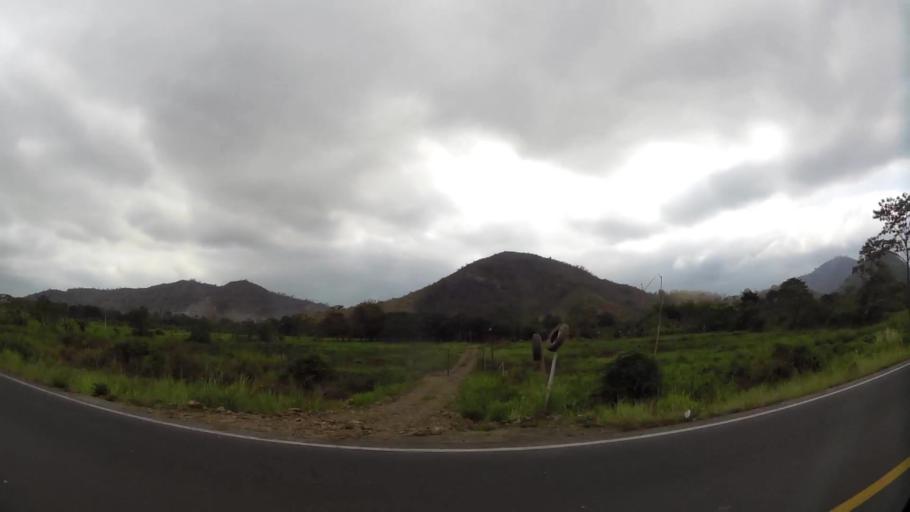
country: EC
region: Guayas
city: Coronel Marcelino Mariduena
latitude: -2.3910
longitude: -79.6305
